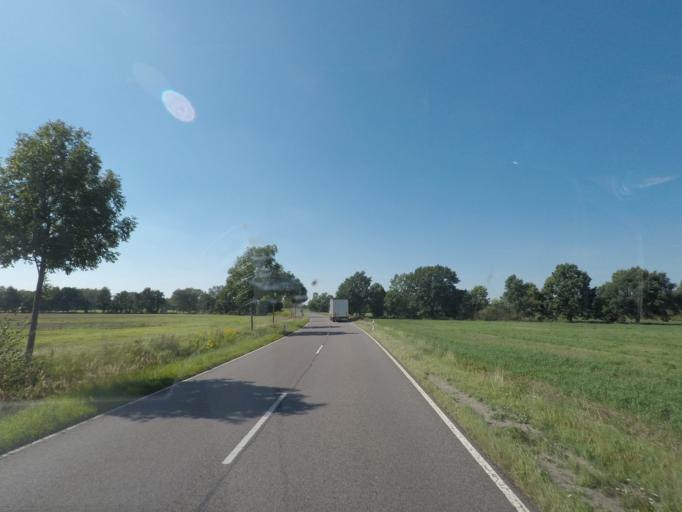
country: DE
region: Brandenburg
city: Welzow
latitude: 51.5743
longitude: 14.0917
